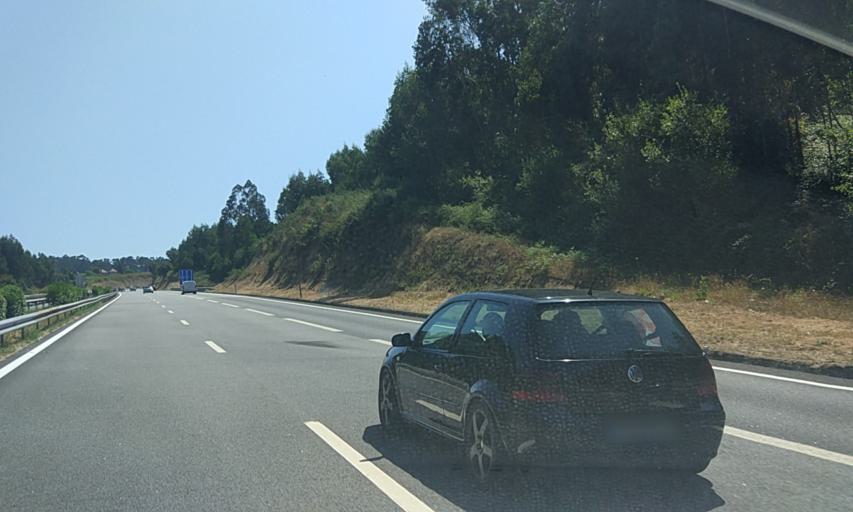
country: PT
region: Porto
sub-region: Penafiel
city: Penafiel
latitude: 41.2153
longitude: -8.2682
